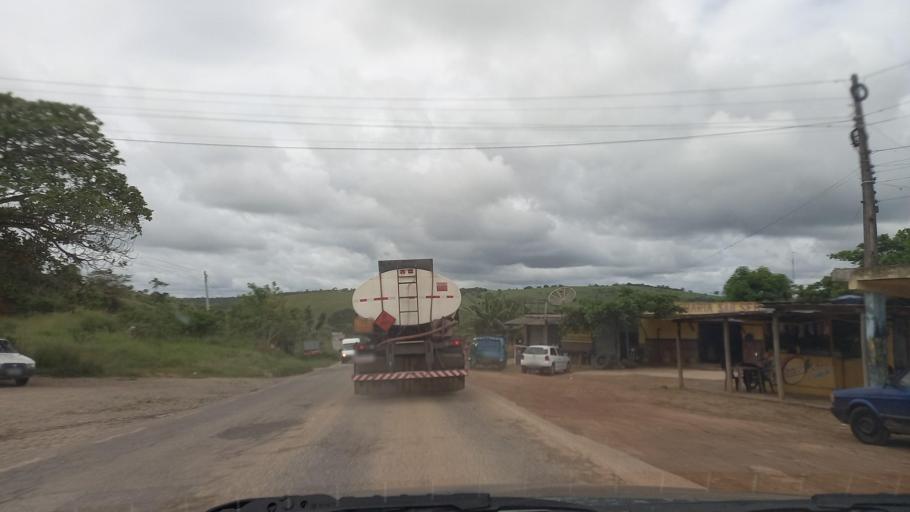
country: BR
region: Pernambuco
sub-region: Canhotinho
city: Canhotinho
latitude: -8.8724
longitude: -36.1992
